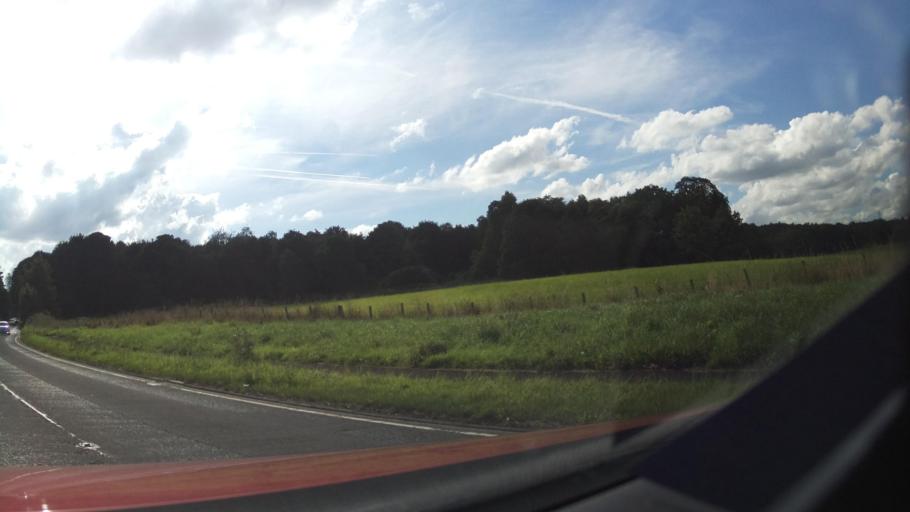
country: GB
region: Scotland
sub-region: Stirling
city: Cowie
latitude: 56.0471
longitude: -3.8571
